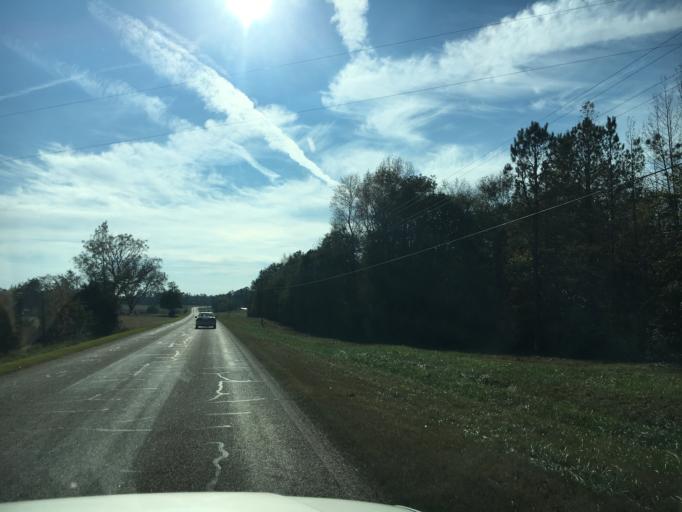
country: US
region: Georgia
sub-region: Hart County
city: Hartwell
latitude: 34.2950
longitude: -82.8401
